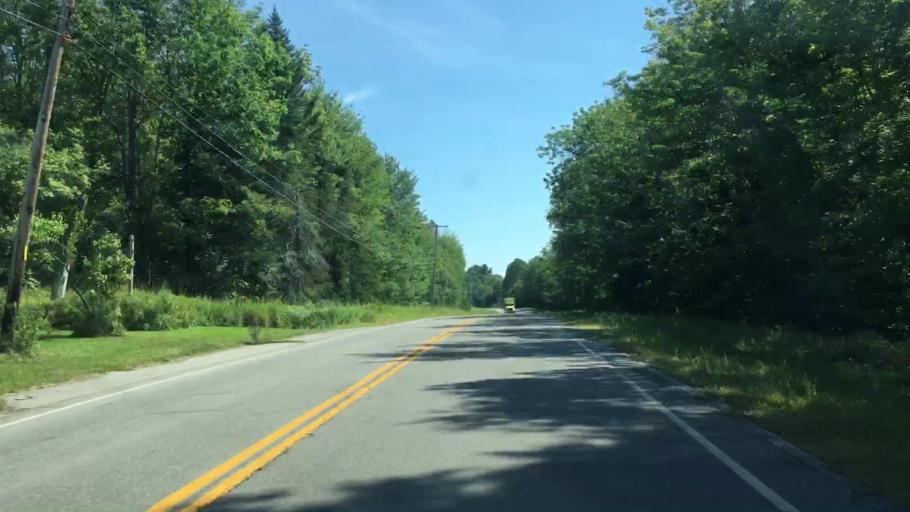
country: US
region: Maine
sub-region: Piscataquis County
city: Milo
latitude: 45.1971
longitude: -68.9039
